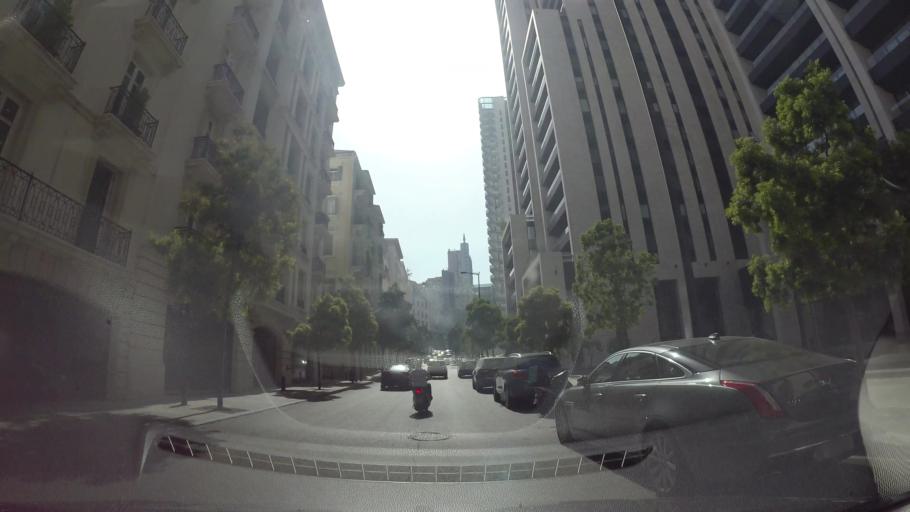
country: LB
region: Beyrouth
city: Beirut
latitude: 33.8987
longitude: 35.4975
